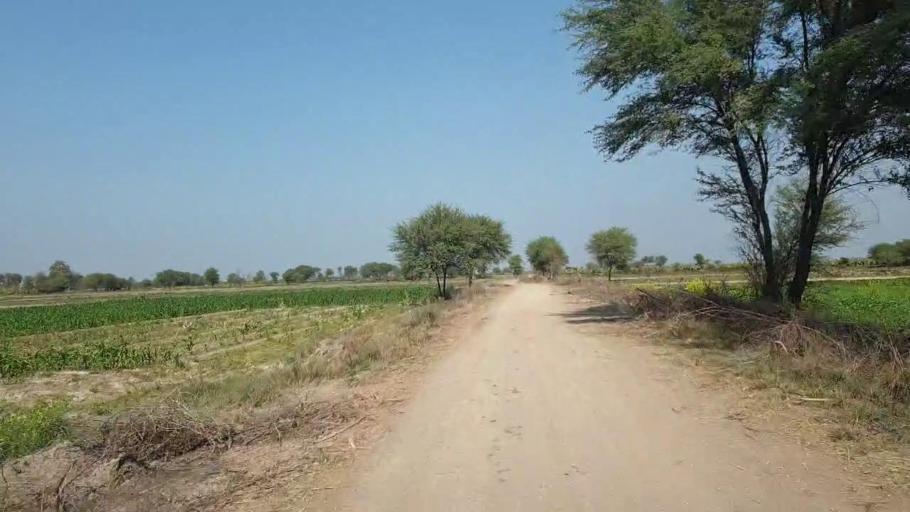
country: PK
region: Sindh
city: Hala
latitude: 25.9581
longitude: 68.4338
